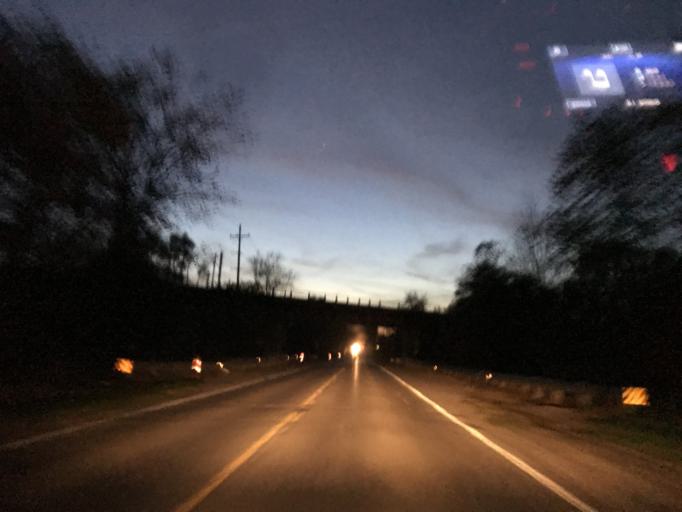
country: US
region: Michigan
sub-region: Oakland County
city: South Lyon
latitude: 42.4330
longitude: -83.6136
